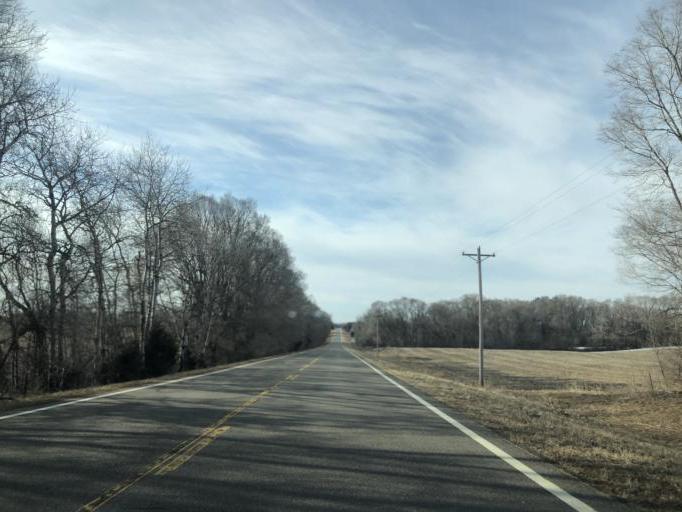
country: US
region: Minnesota
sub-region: Sherburne County
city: Becker
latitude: 45.4142
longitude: -93.8501
